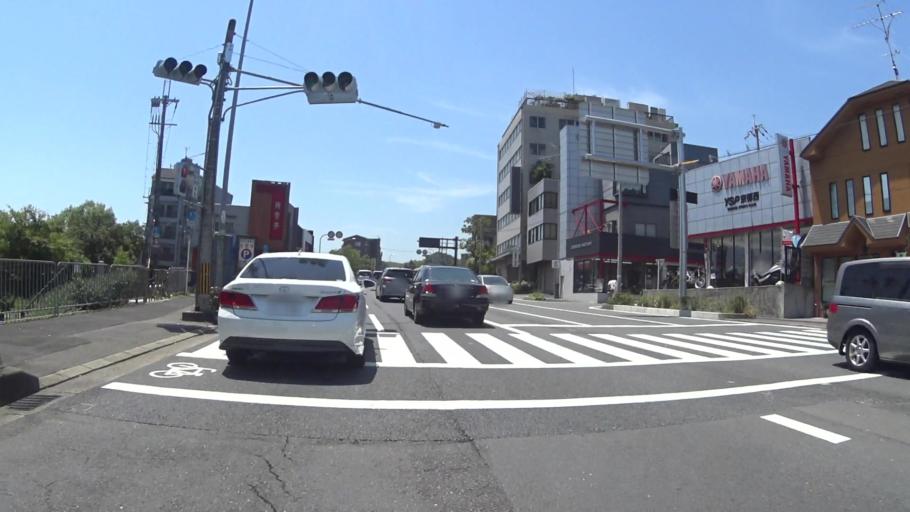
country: JP
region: Kyoto
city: Muko
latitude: 34.9773
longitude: 135.6888
